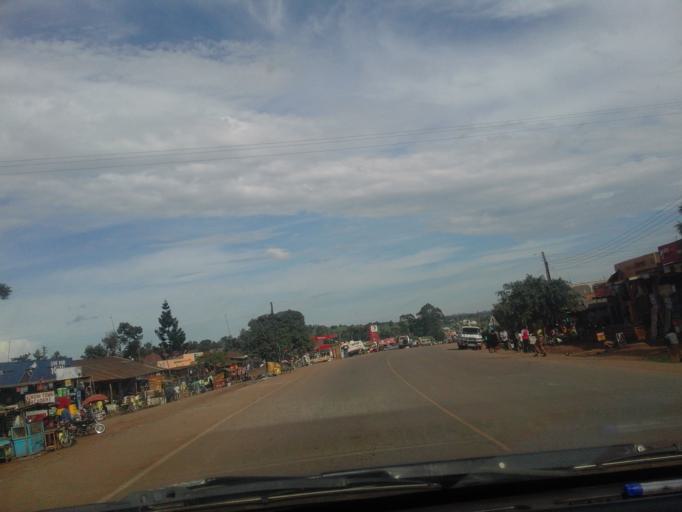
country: UG
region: Central Region
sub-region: Lwengo District
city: Lwengo
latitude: -0.3531
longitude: 31.5523
